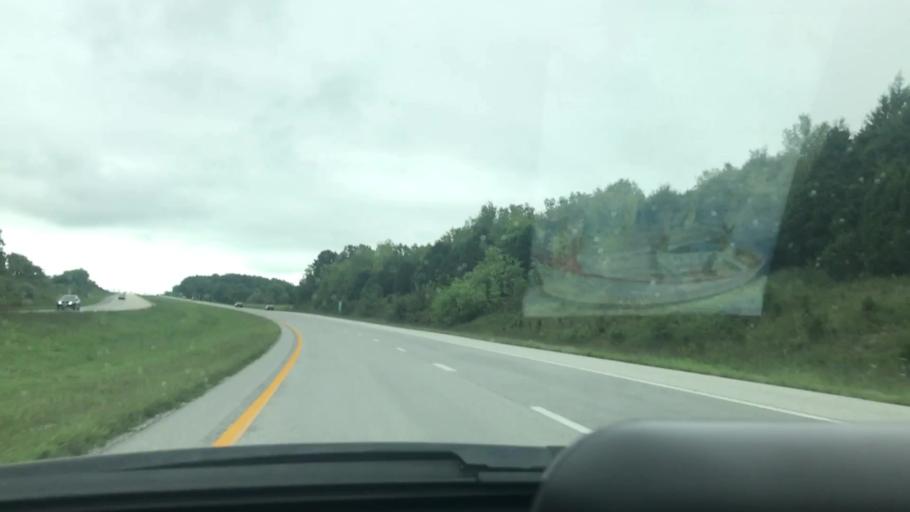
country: US
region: Missouri
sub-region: Greene County
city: Strafford
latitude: 37.2916
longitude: -93.1815
